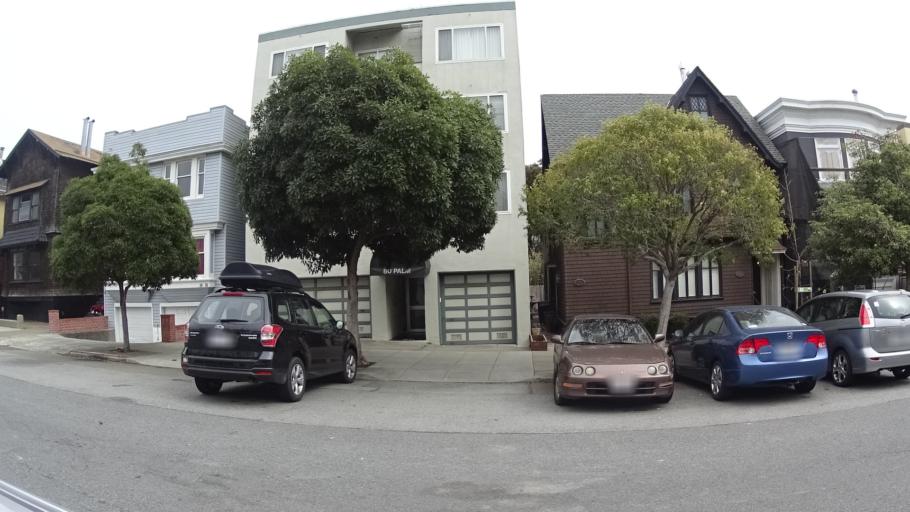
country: US
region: California
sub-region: San Francisco County
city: San Francisco
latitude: 37.7843
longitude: -122.4580
